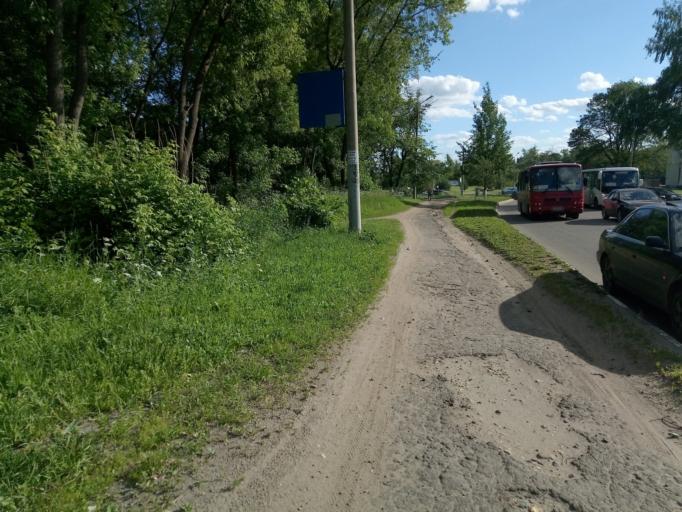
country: RU
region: Jaroslavl
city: Yaroslavl
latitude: 57.6451
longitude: 39.9208
